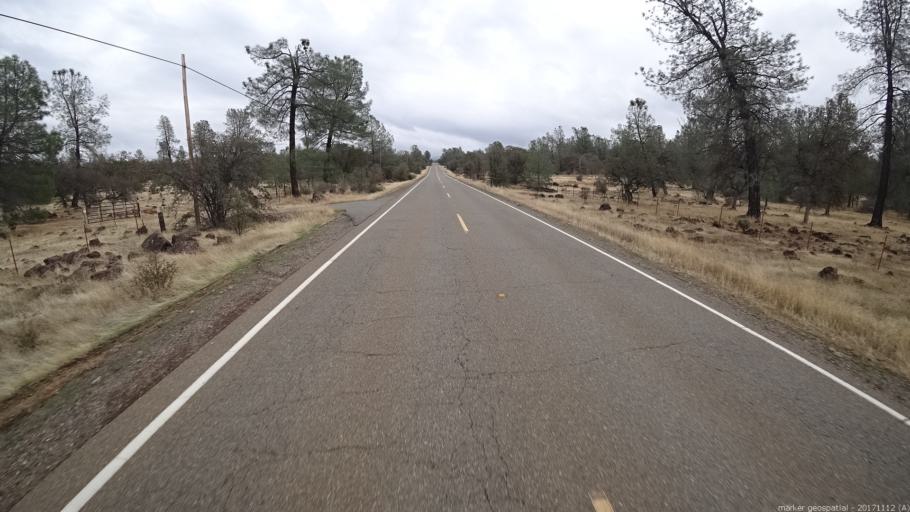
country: US
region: California
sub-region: Shasta County
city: Palo Cedro
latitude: 40.4812
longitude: -122.0973
